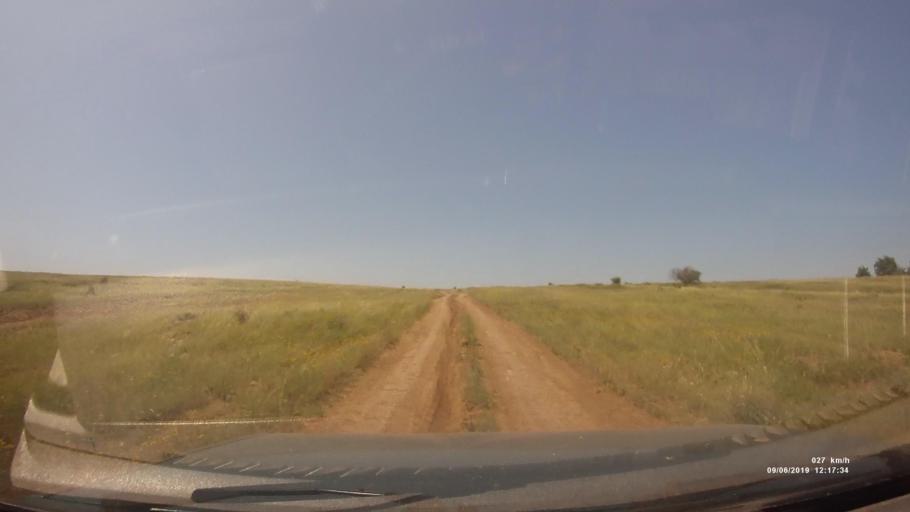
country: RU
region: Rostov
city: Staraya Stanitsa
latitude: 48.2556
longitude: 40.3146
